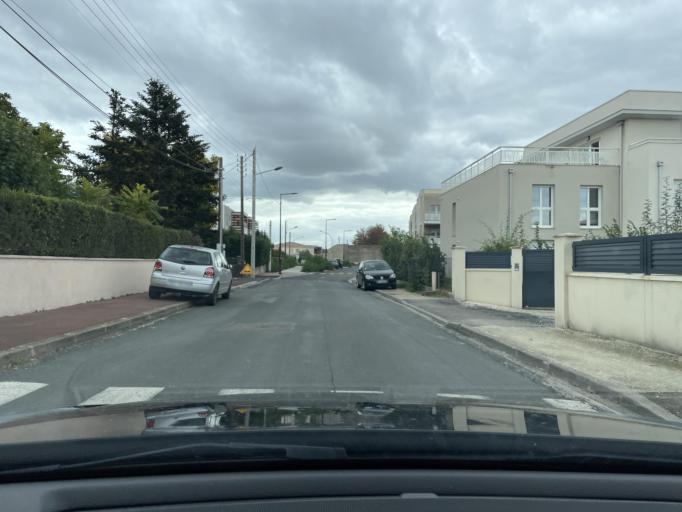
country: FR
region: Aquitaine
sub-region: Departement de la Gironde
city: Le Bouscat
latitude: 44.8792
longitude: -0.5930
